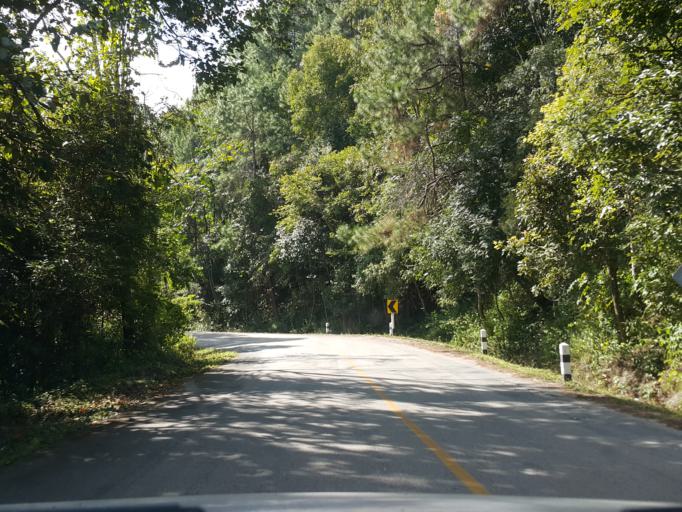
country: TH
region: Mae Hong Son
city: Mae Hi
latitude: 19.2522
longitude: 98.6438
